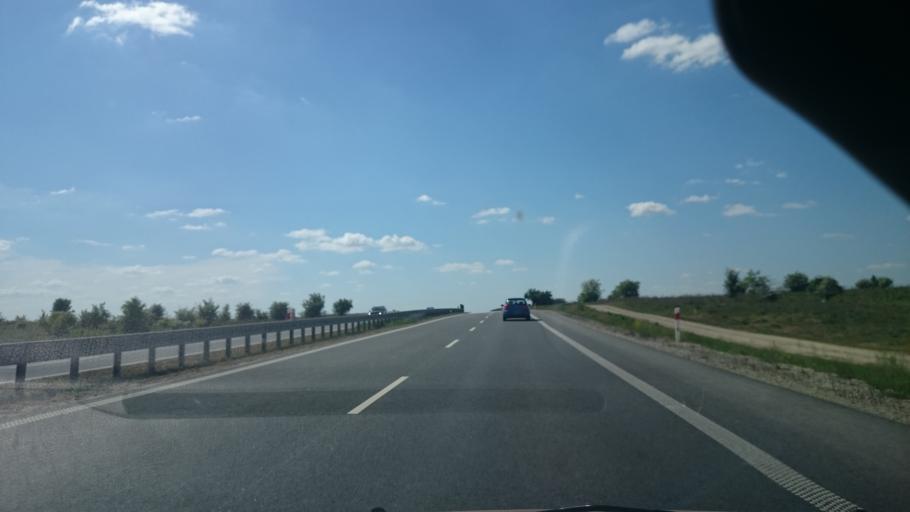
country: PL
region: Opole Voivodeship
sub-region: Powiat nyski
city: Nysa
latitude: 50.5008
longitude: 17.3110
